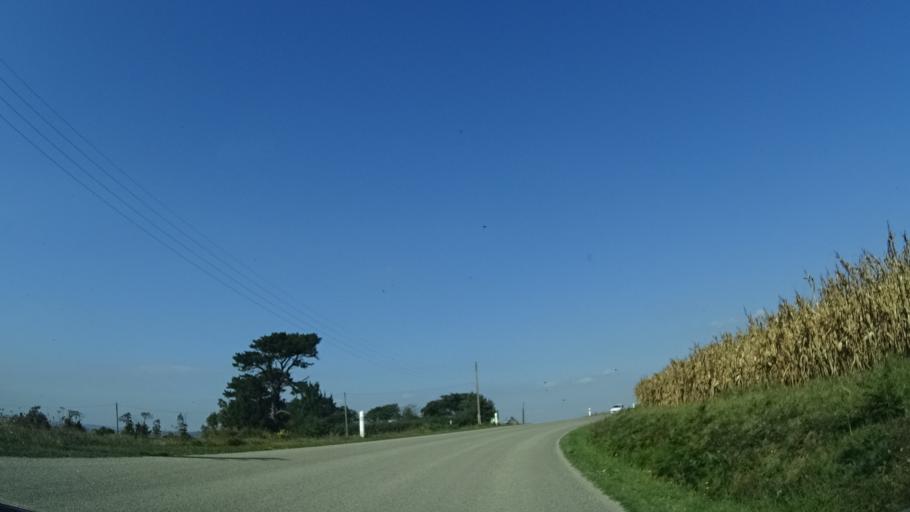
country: FR
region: Brittany
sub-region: Departement du Finistere
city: Plonevez-Porzay
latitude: 48.1176
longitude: -4.2393
